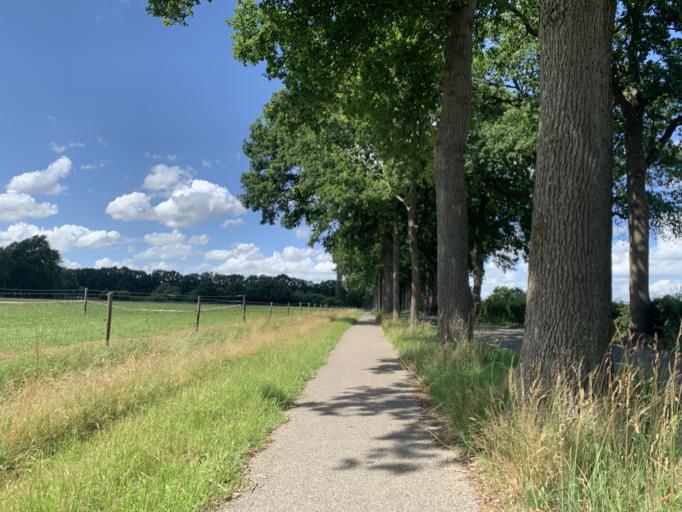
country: NL
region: Drenthe
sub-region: Gemeente Tynaarlo
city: Zuidlaren
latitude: 53.1339
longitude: 6.6567
